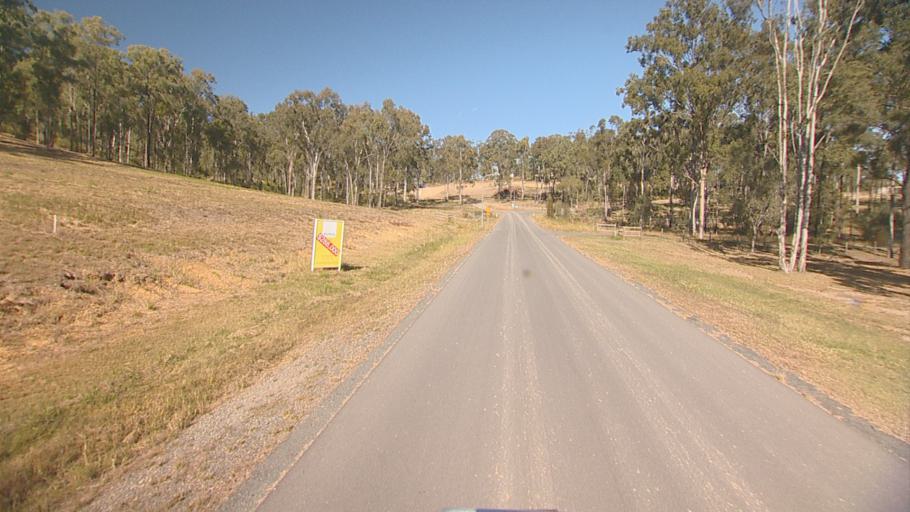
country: AU
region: Queensland
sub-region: Logan
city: Windaroo
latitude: -27.7735
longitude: 153.1459
